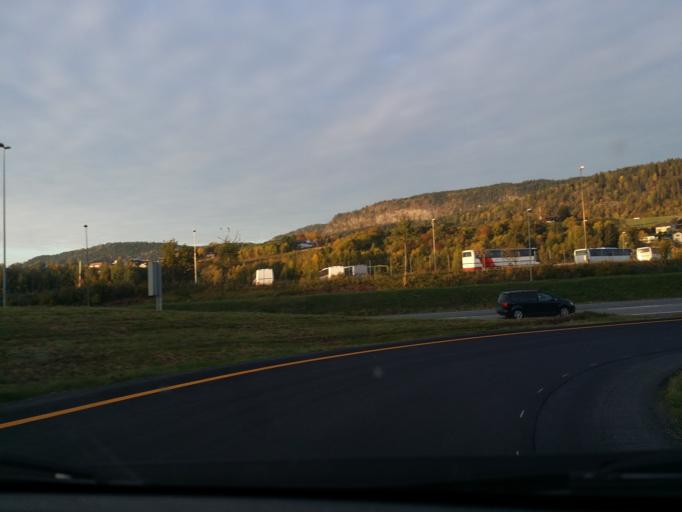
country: NO
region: Akershus
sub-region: Baerum
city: Skui
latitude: 59.9233
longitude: 10.4640
